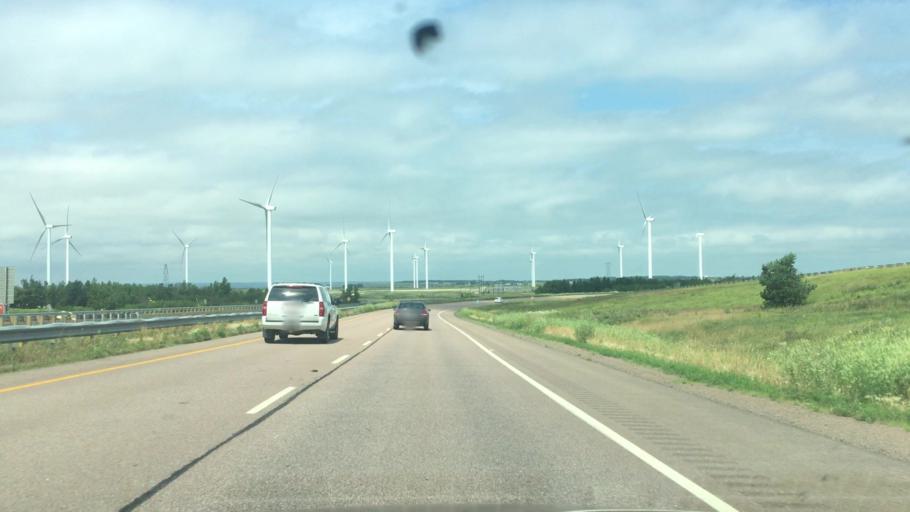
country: CA
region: Nova Scotia
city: Amherst
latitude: 45.8190
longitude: -64.2348
